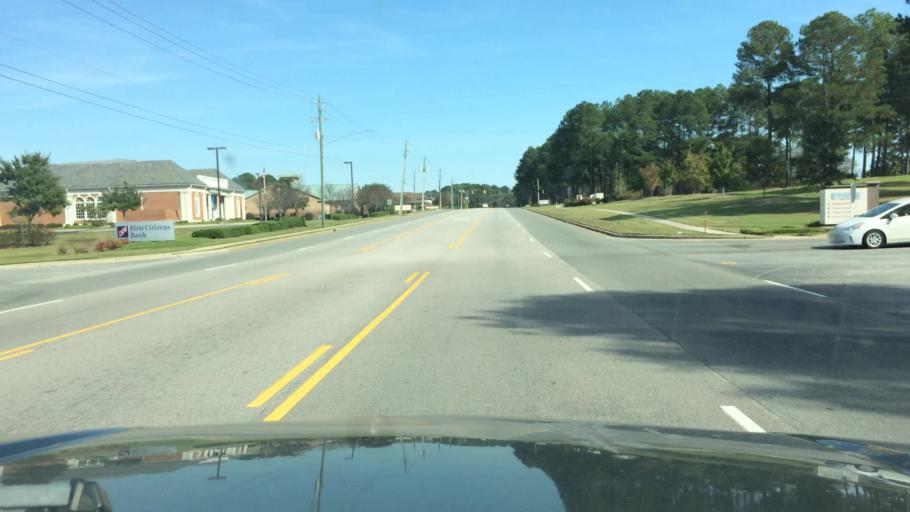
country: US
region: North Carolina
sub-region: Wayne County
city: Goldsboro
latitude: 35.3998
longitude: -77.9564
